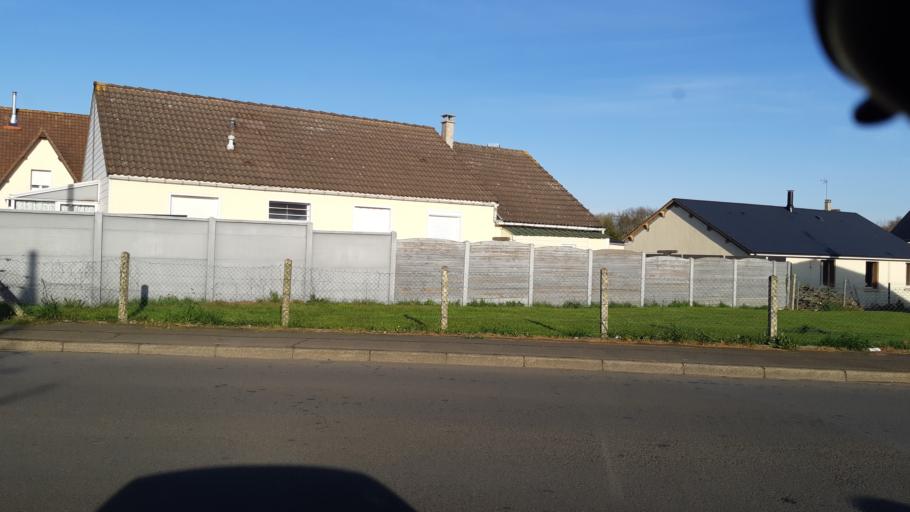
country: FR
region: Lower Normandy
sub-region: Departement de la Manche
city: Saint-Pair-sur-Mer
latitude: 48.8368
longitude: -1.5612
